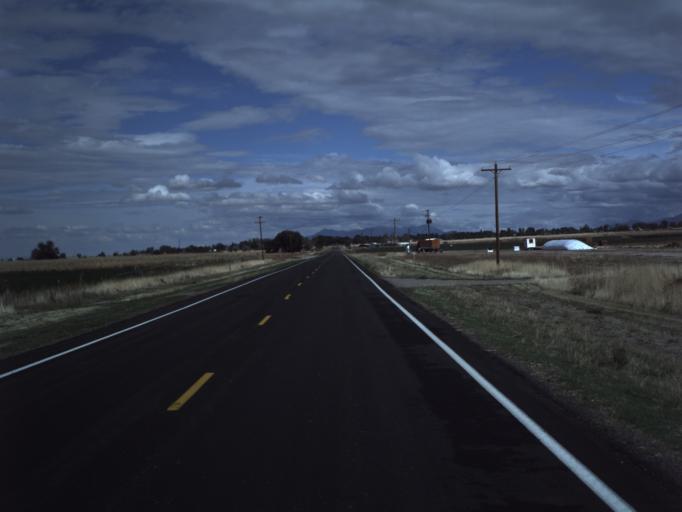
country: US
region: Utah
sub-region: Millard County
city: Fillmore
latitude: 38.8678
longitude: -112.4162
